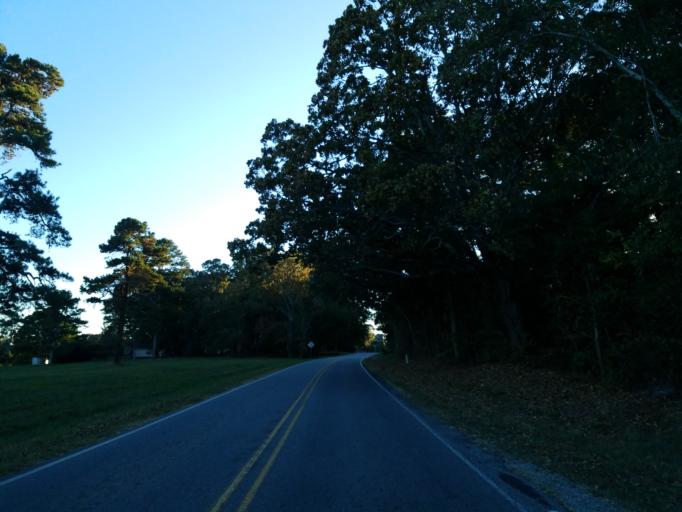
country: US
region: Georgia
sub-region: Forsyth County
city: Cumming
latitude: 34.2782
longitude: -84.0811
